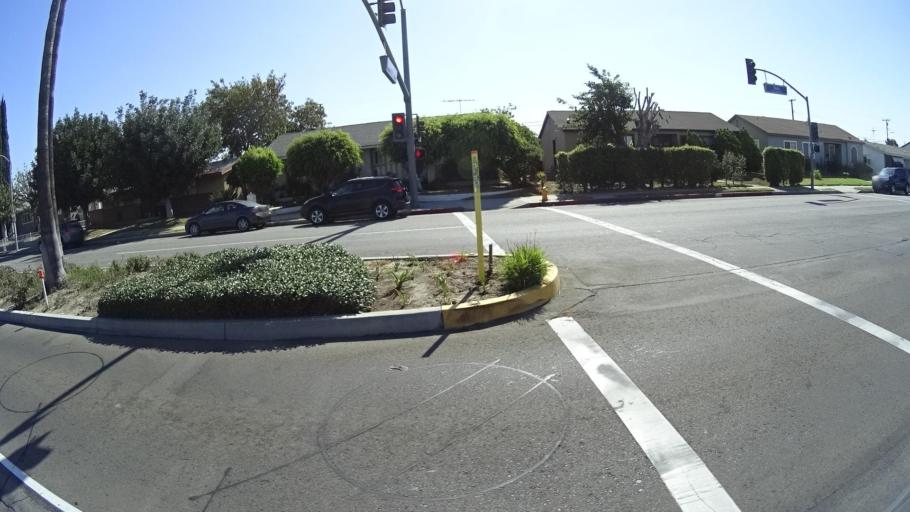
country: US
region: California
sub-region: Orange County
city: Buena Park
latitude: 33.8437
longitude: -117.9849
